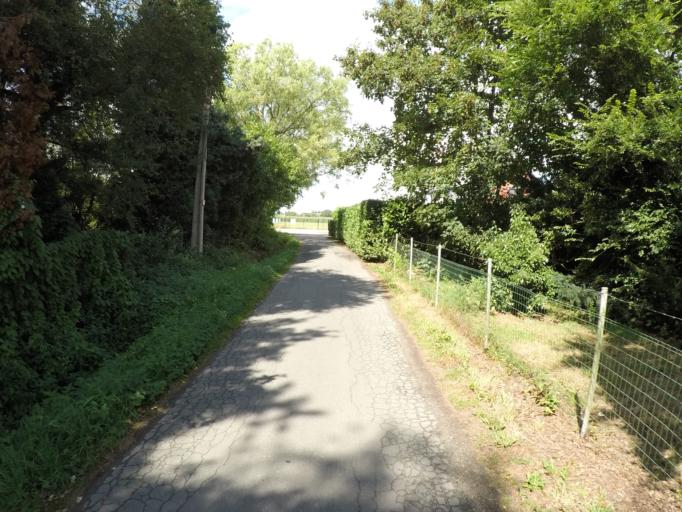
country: BE
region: Flanders
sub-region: Provincie Antwerpen
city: Wommelgem
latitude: 51.1889
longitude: 4.5321
